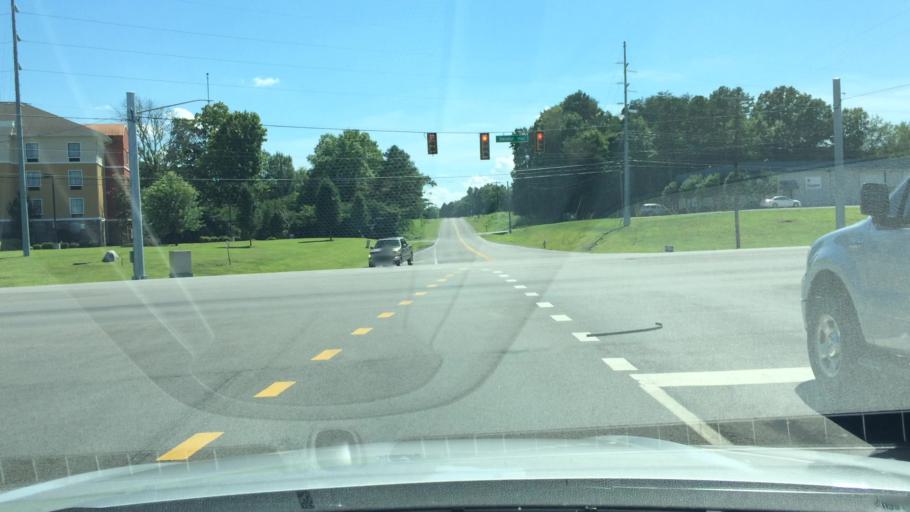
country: US
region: Tennessee
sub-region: McMinn County
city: Athens
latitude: 35.4685
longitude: -84.6521
